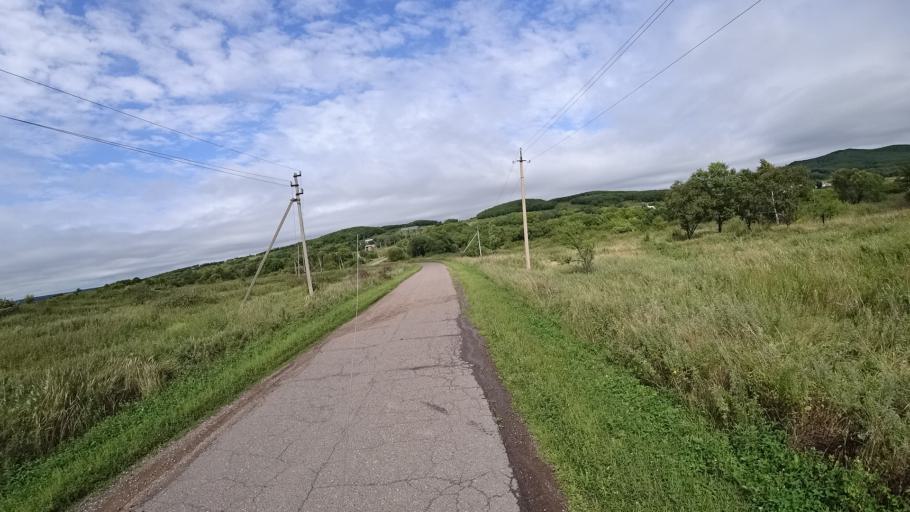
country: RU
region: Primorskiy
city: Lyalichi
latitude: 44.1339
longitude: 132.3879
